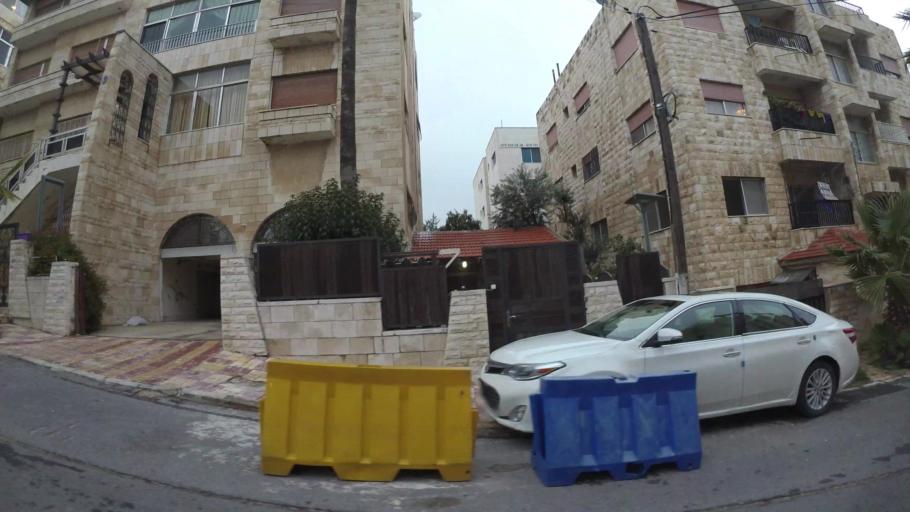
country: JO
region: Amman
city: Amman
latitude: 31.9670
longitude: 35.8844
